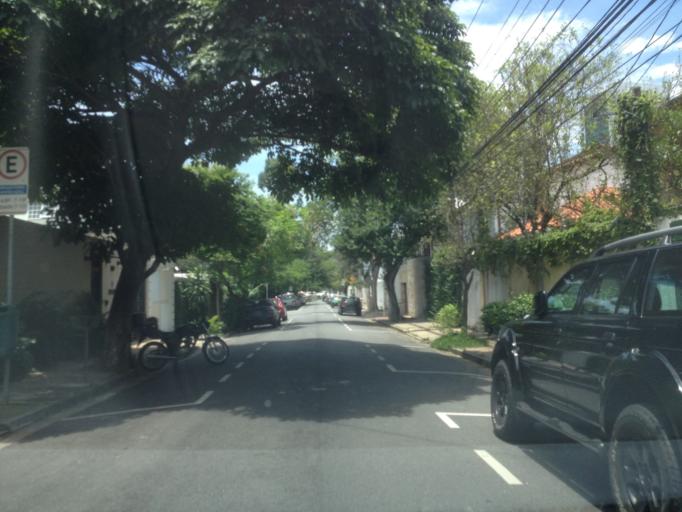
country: BR
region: Sao Paulo
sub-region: Sao Paulo
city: Sao Paulo
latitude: -23.5730
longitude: -46.6925
